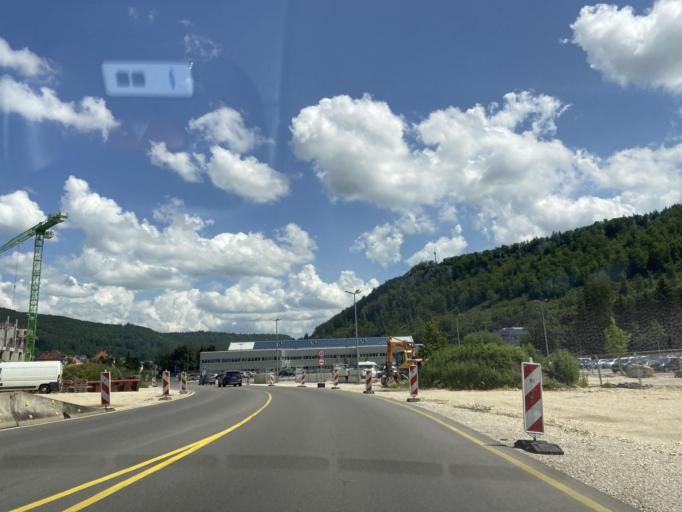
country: DE
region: Baden-Wuerttemberg
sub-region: Tuebingen Region
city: Albstadt
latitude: 48.2081
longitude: 9.0262
